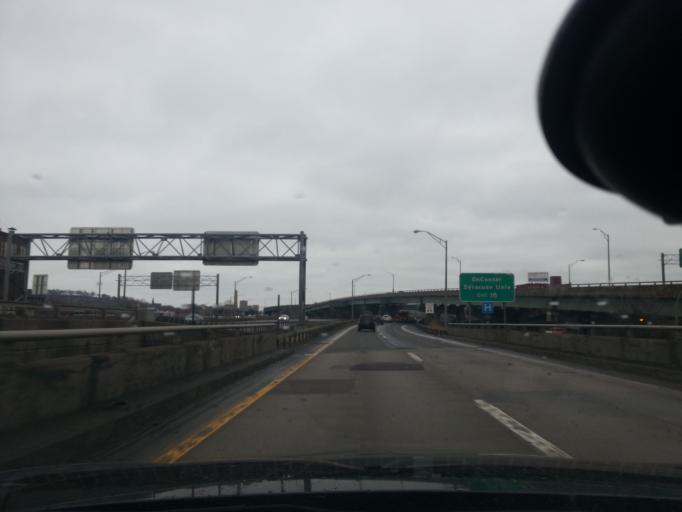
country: US
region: New York
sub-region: Onondaga County
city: Syracuse
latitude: 43.0515
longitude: -76.1478
